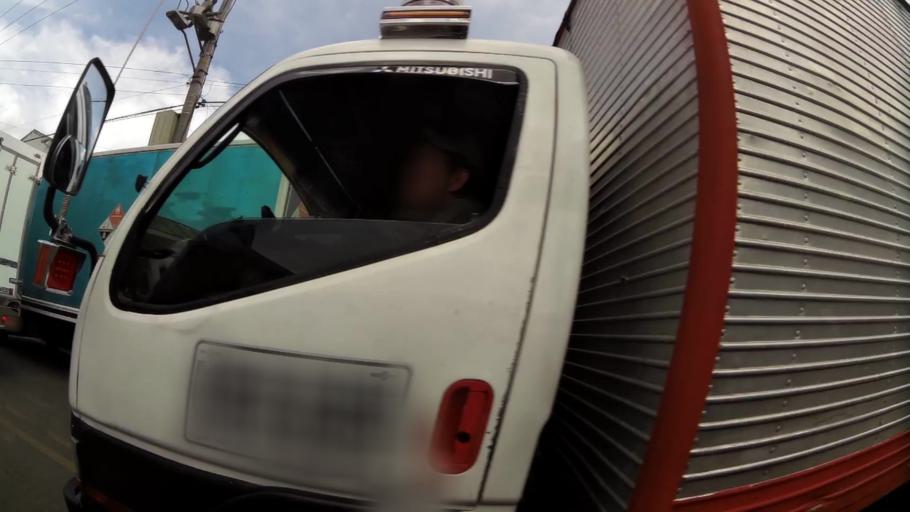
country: CO
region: Bogota D.C.
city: Bogota
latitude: 4.6541
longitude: -74.1335
